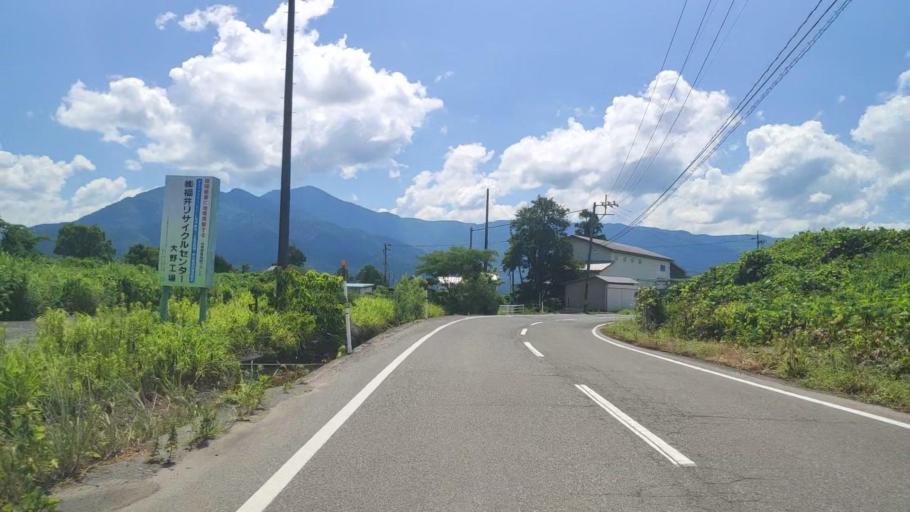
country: JP
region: Fukui
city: Ono
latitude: 35.9739
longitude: 136.5234
